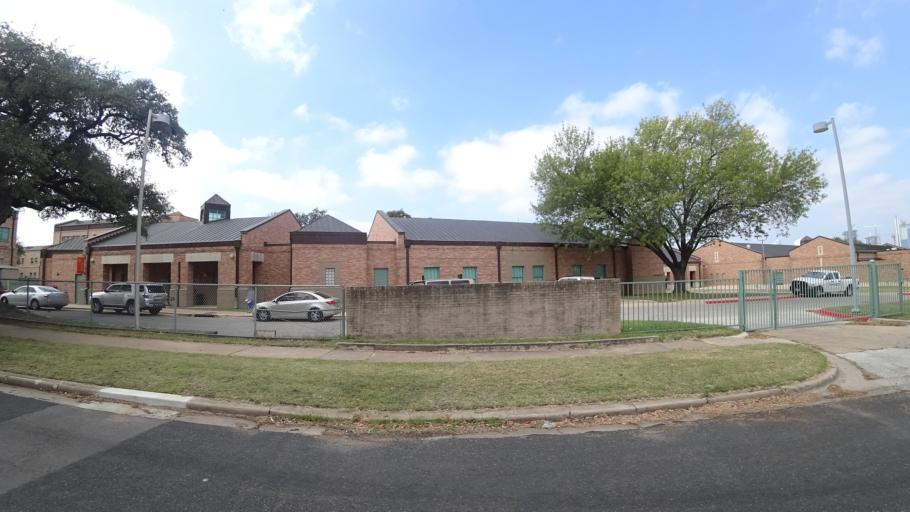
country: US
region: Texas
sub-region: Travis County
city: Austin
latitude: 30.2525
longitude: -97.7500
